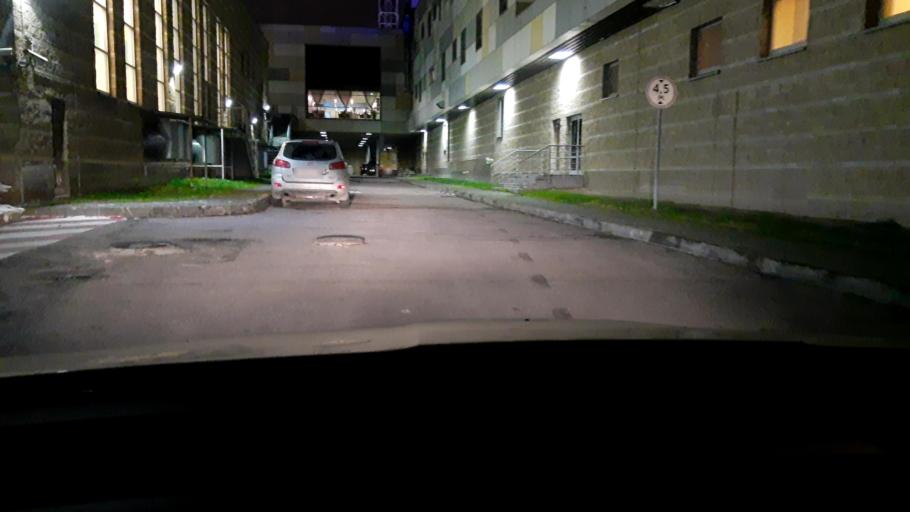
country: RU
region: Moscow
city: Yasenevo
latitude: 55.5975
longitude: 37.5282
